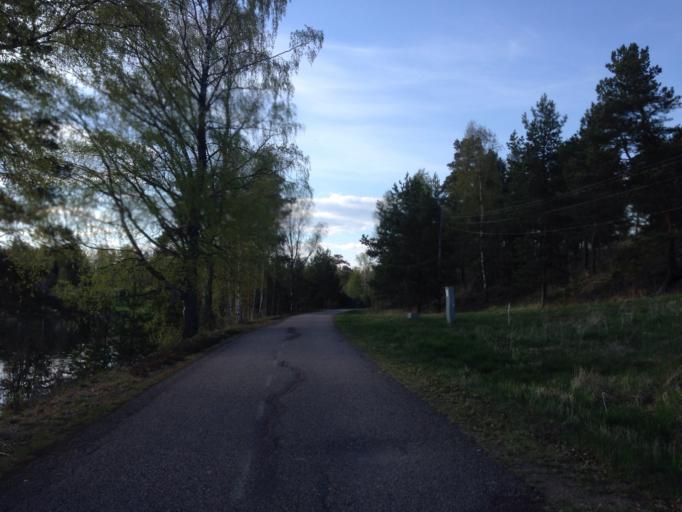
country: SE
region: Dalarna
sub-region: Ludvika Kommun
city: Ludvika
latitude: 60.1638
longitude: 15.1635
